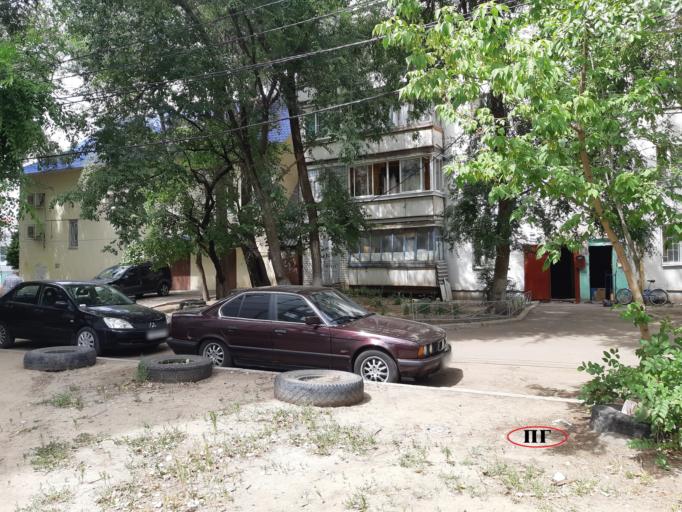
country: RU
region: Voronezj
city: Podgornoye
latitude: 51.7052
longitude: 39.1566
